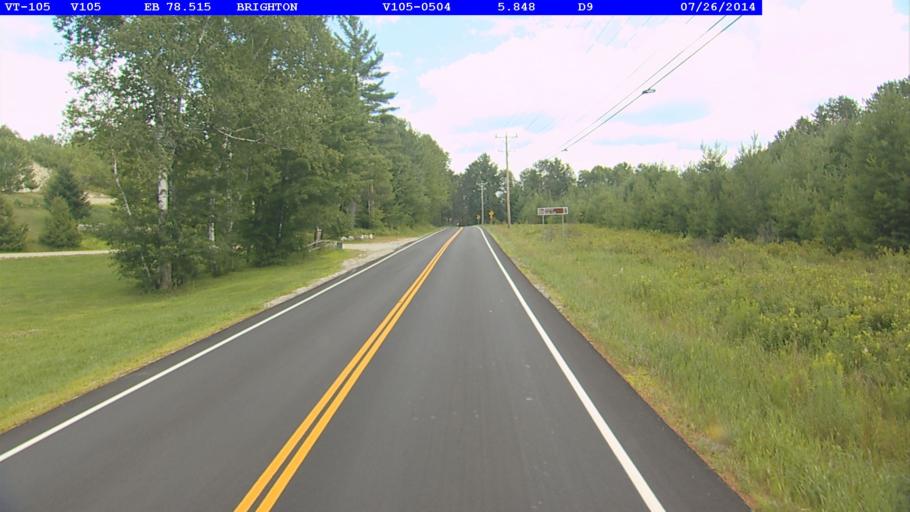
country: US
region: Vermont
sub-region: Caledonia County
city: Lyndonville
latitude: 44.8083
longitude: -71.8578
